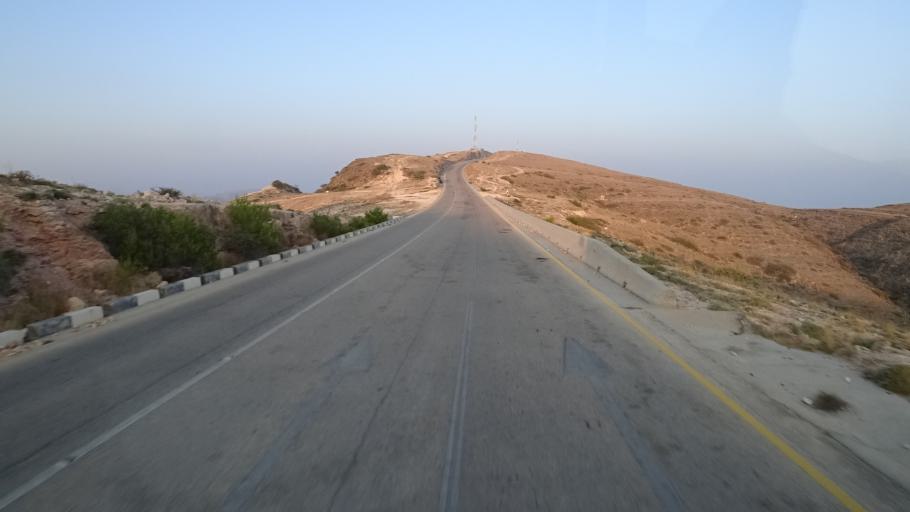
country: OM
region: Zufar
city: Salalah
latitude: 16.8212
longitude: 53.6411
